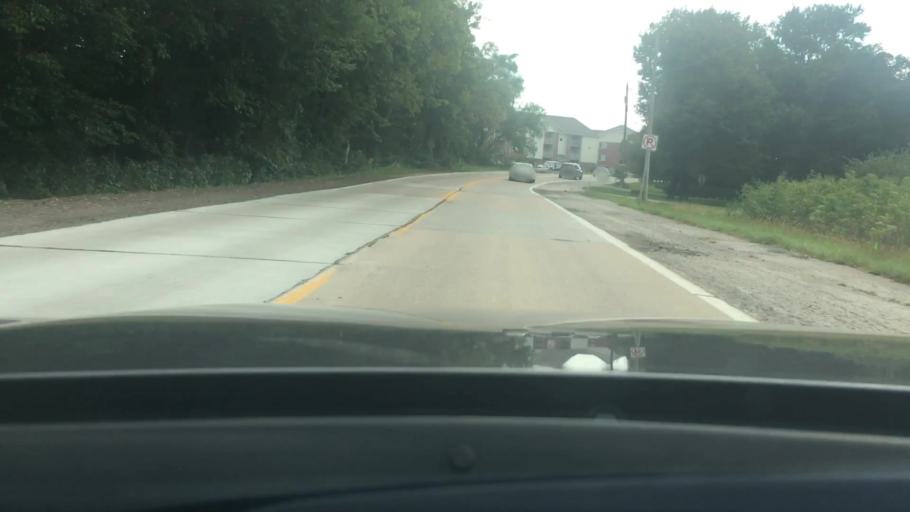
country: US
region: Iowa
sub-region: Pottawattamie County
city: Council Bluffs
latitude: 41.2547
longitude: -95.8098
